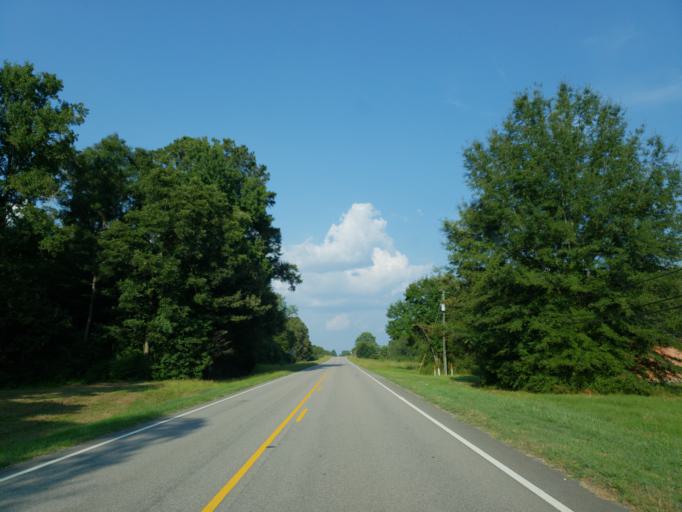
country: US
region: Alabama
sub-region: Greene County
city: Eutaw
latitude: 32.7556
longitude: -88.0263
